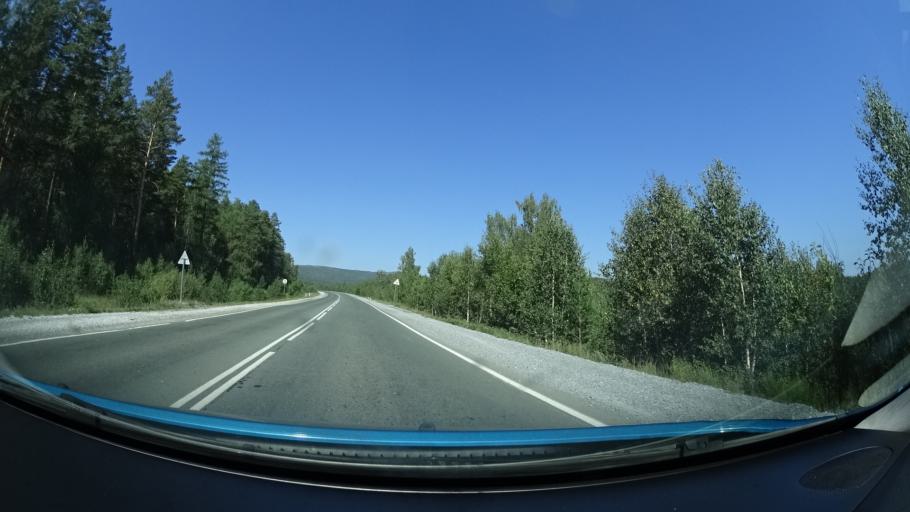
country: RU
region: Bashkortostan
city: Abzakovo
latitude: 53.8545
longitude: 58.5777
